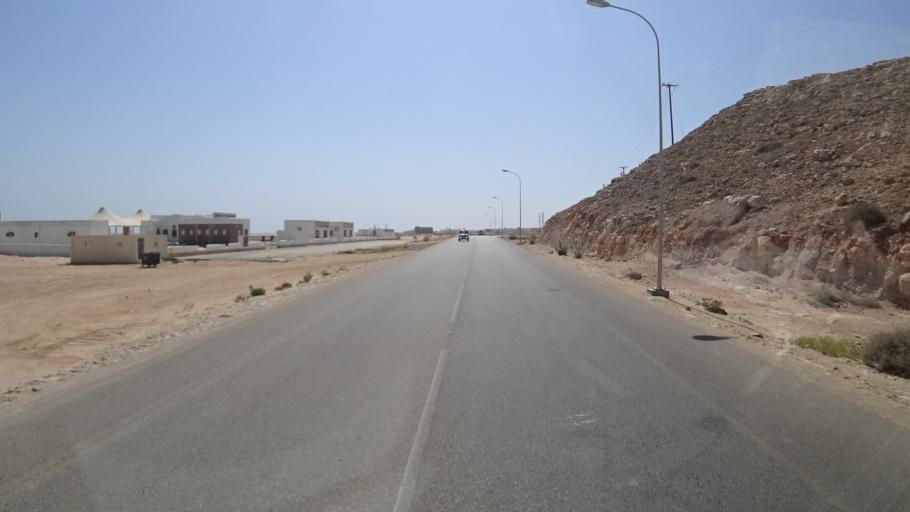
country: OM
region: Ash Sharqiyah
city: Sur
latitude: 22.5653
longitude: 59.5747
